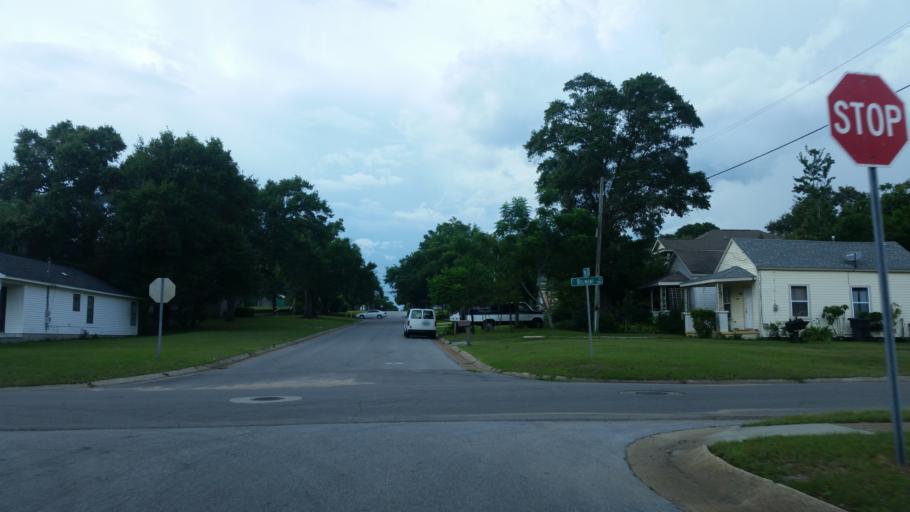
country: US
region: Florida
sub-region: Escambia County
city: Pensacola
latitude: 30.4194
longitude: -87.2047
